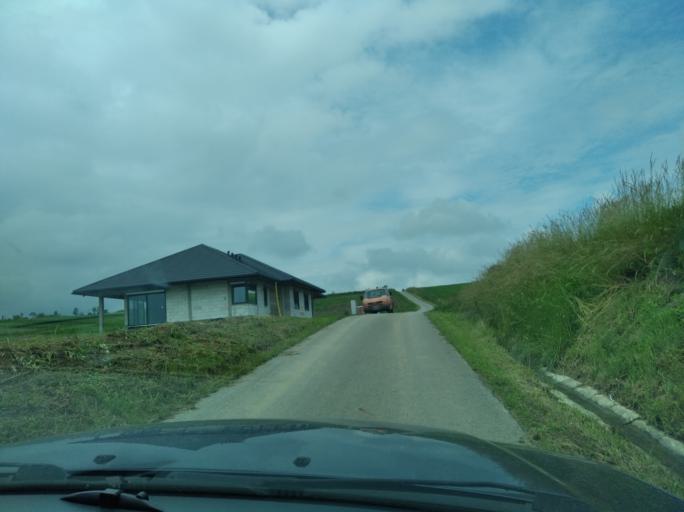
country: PL
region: Subcarpathian Voivodeship
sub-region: Powiat jaroslawski
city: Pruchnik
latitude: 49.9020
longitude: 22.5009
